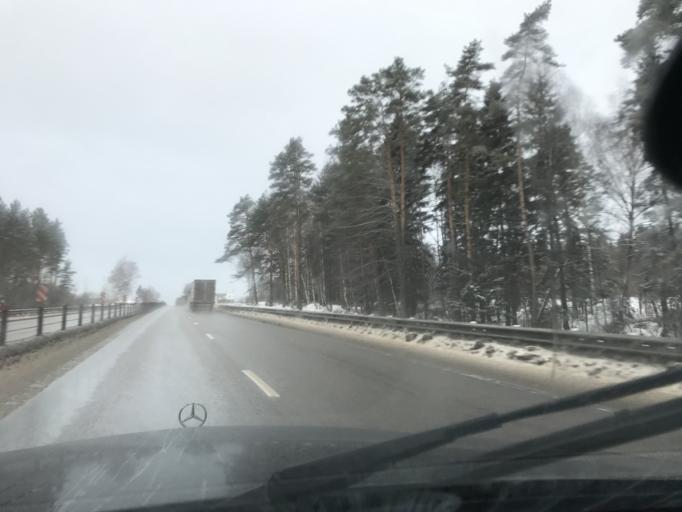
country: RU
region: Vladimir
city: Gorokhovets
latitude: 56.1682
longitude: 42.4550
